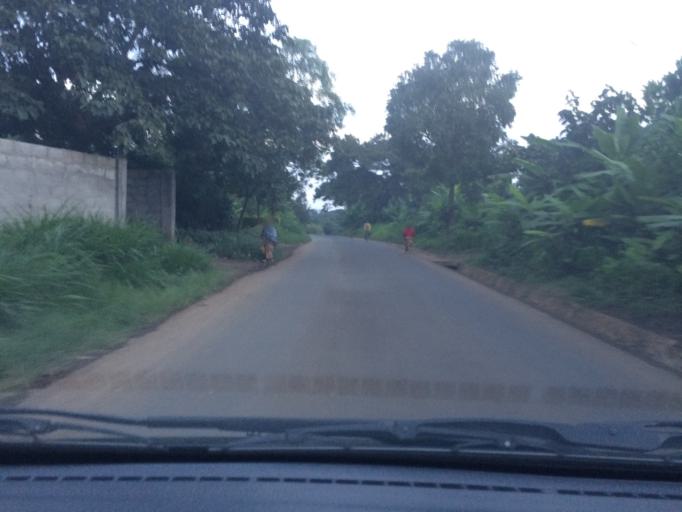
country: TZ
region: Arusha
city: Usa River
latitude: -3.3689
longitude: 36.8166
